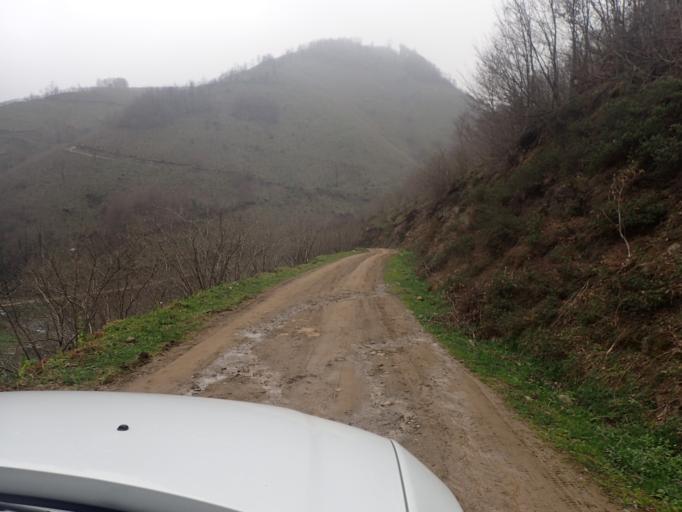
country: TR
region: Ordu
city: Camas
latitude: 40.8992
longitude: 37.5557
